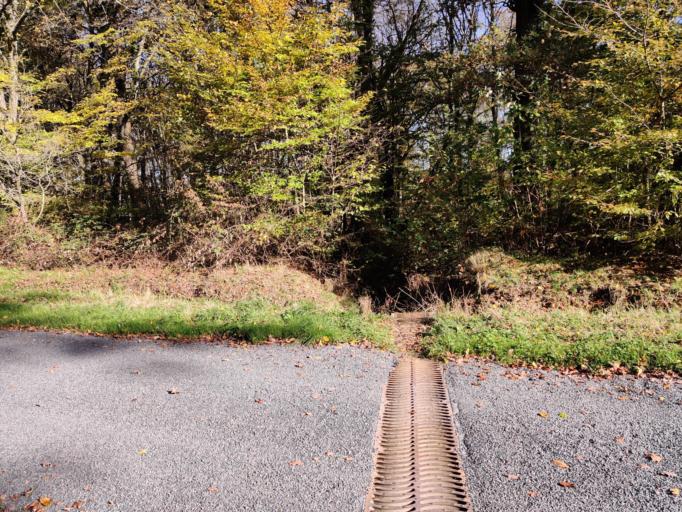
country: FR
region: Centre
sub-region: Departement du Loiret
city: Semoy
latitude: 47.9527
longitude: 1.9351
